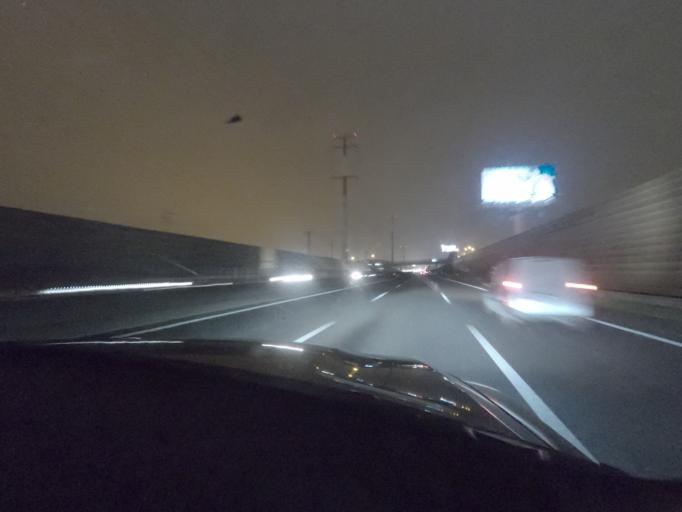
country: PT
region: Lisbon
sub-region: Loures
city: Santa Iria da Azoia
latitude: 38.8367
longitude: -9.0957
